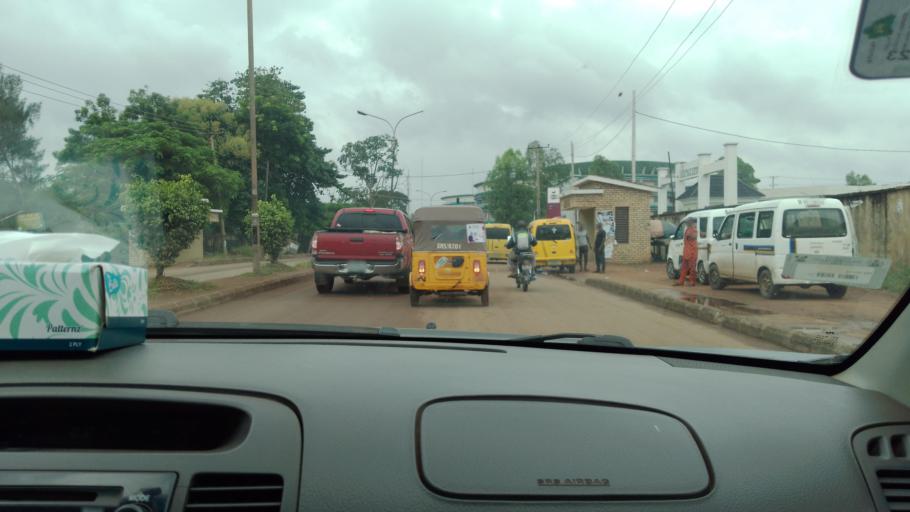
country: NG
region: Enugu
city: Enugu
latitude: 6.4469
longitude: 7.4825
